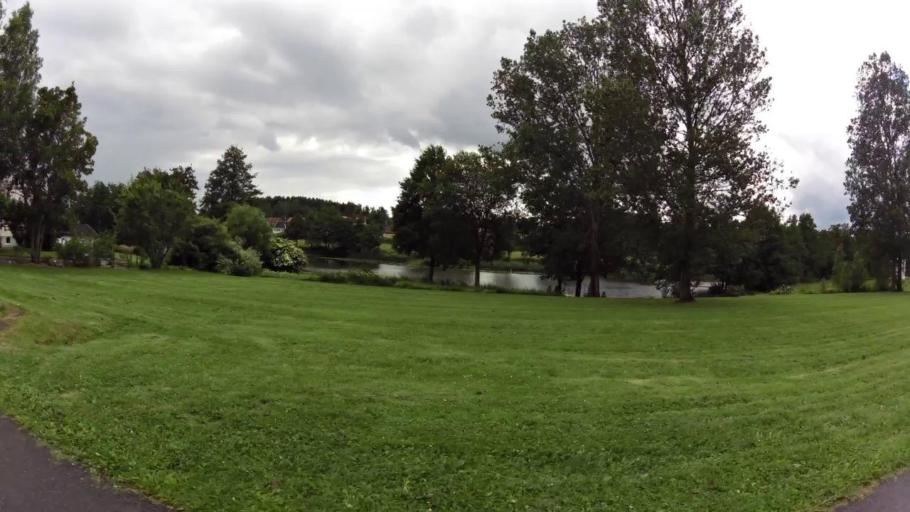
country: SE
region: OEstergoetland
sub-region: Linkopings Kommun
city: Sturefors
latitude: 58.3825
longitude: 15.7050
